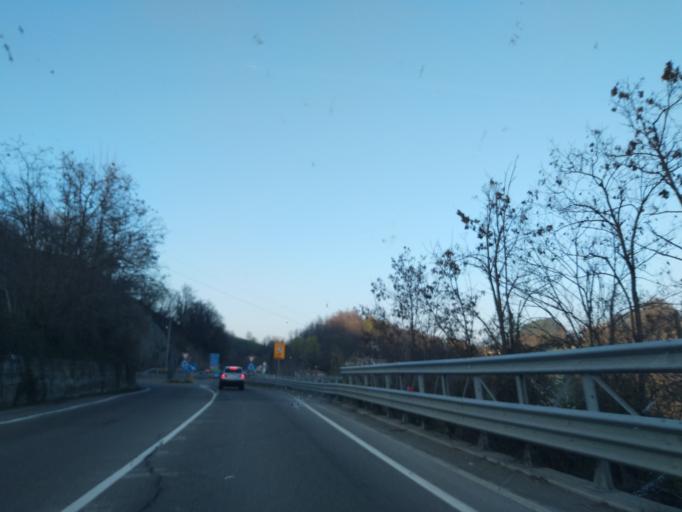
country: IT
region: Emilia-Romagna
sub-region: Provincia di Reggio Emilia
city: Felina
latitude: 44.4461
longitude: 10.4475
